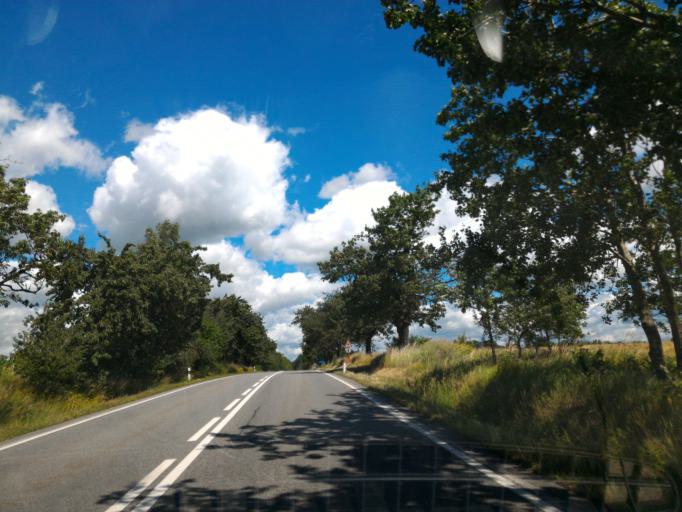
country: CZ
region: Vysocina
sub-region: Okres Jihlava
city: Telc
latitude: 49.2066
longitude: 15.4531
